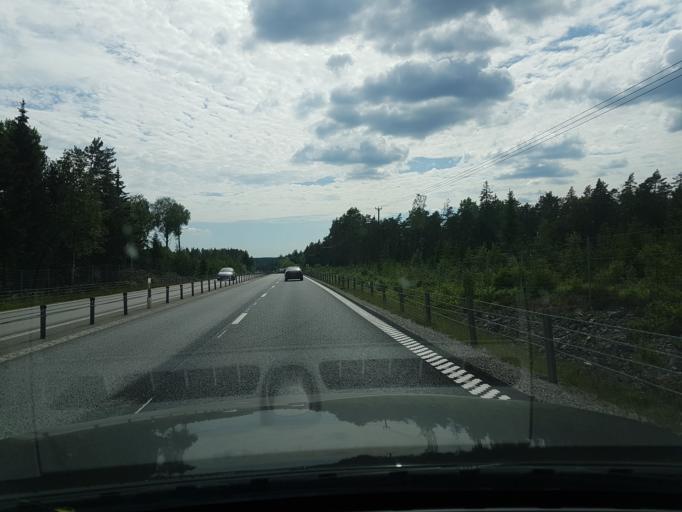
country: SE
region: Stockholm
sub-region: Osterakers Kommun
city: Akersberga
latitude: 59.5819
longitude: 18.2475
